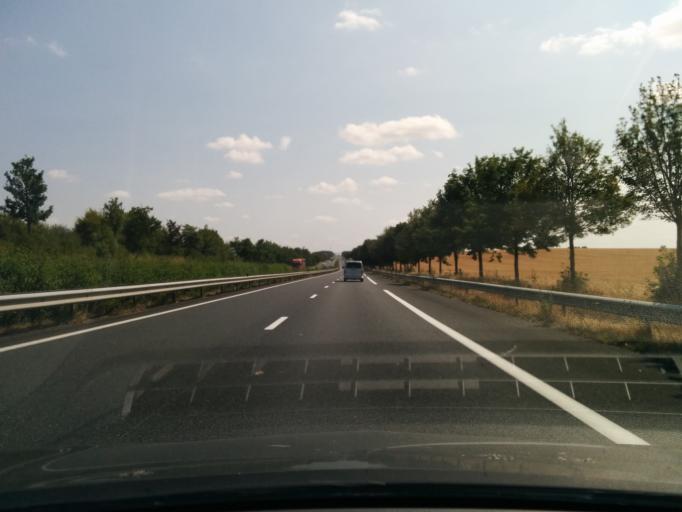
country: FR
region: Centre
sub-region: Departement de l'Indre
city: Vatan
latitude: 47.0138
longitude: 1.7830
